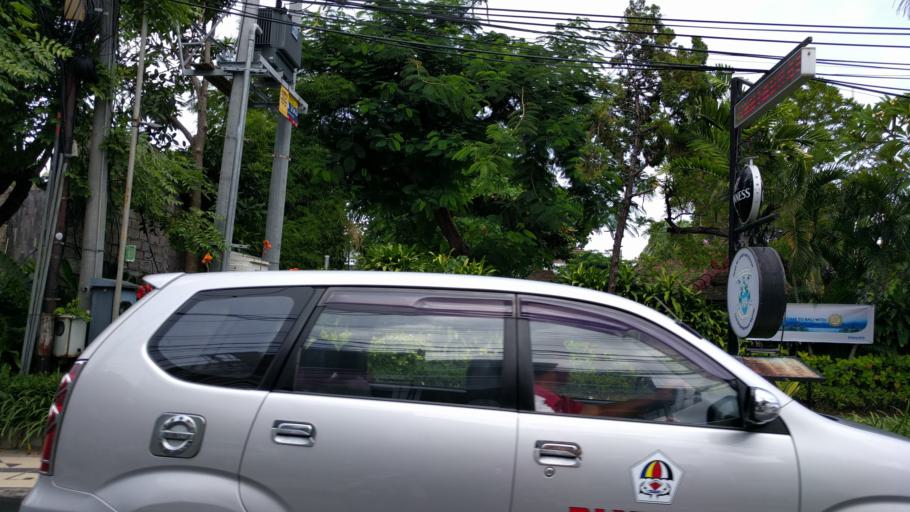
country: ID
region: Bali
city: Jabajero
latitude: -8.7323
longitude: 115.1674
